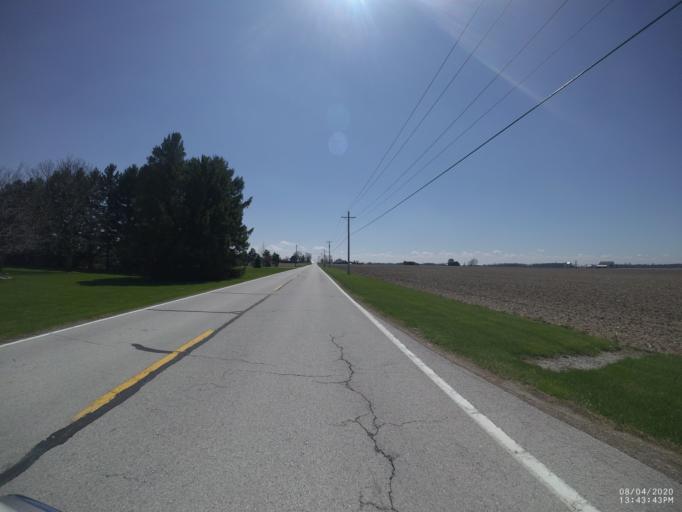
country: US
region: Ohio
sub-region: Sandusky County
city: Gibsonburg
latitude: 41.3326
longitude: -83.3058
